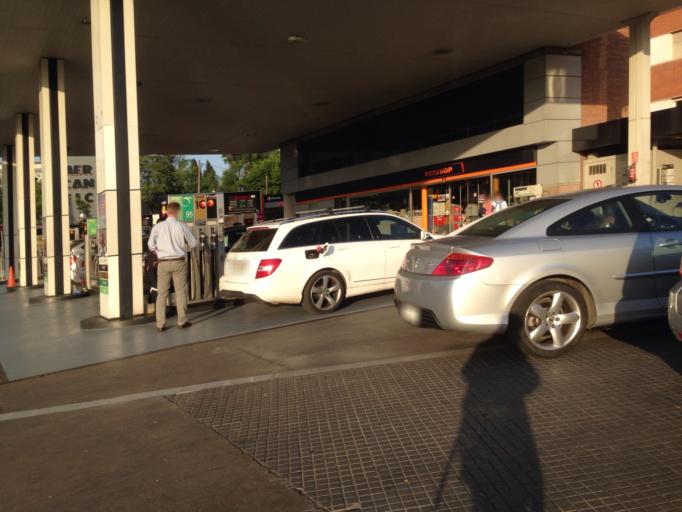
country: ES
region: Catalonia
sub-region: Provincia de Barcelona
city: Sant Cugat del Valles
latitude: 41.4778
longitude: 2.0693
